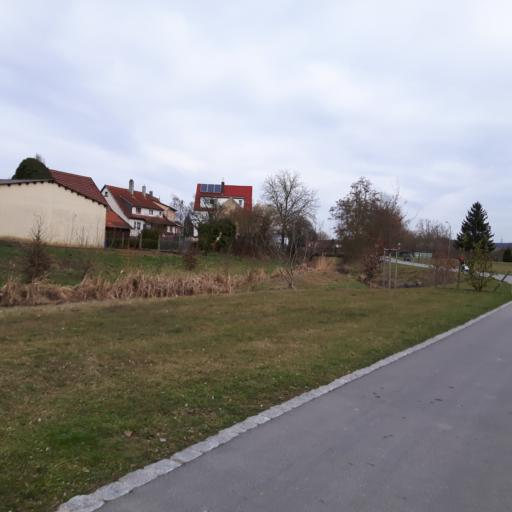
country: DE
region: Baden-Wuerttemberg
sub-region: Regierungsbezirk Stuttgart
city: Ilsfeld
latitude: 49.0536
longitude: 9.2503
